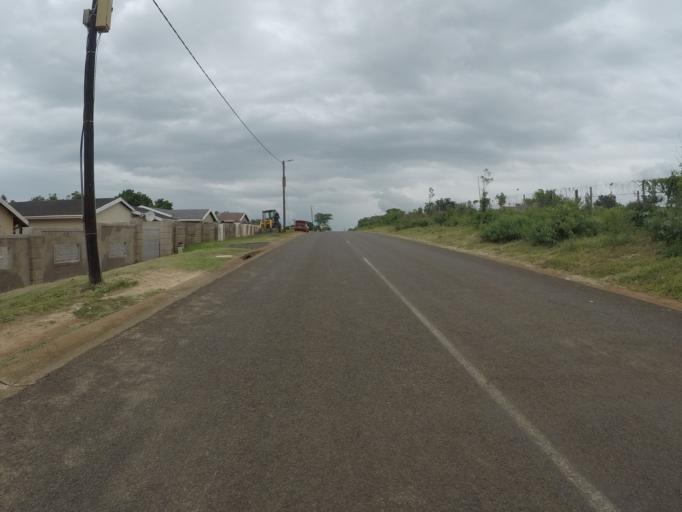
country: ZA
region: KwaZulu-Natal
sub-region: uThungulu District Municipality
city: Empangeni
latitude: -28.7786
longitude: 31.8535
